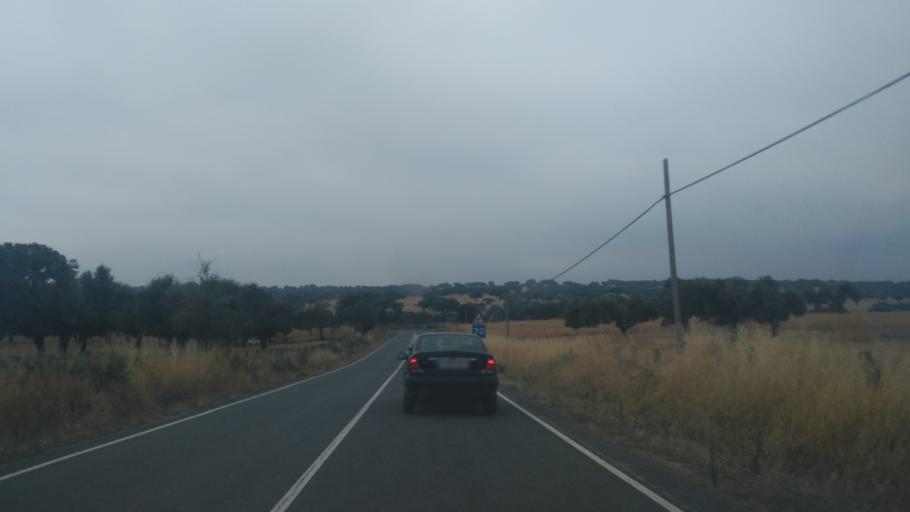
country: ES
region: Castille and Leon
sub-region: Provincia de Salamanca
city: Robliza de Cojos
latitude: 40.8541
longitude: -5.9602
